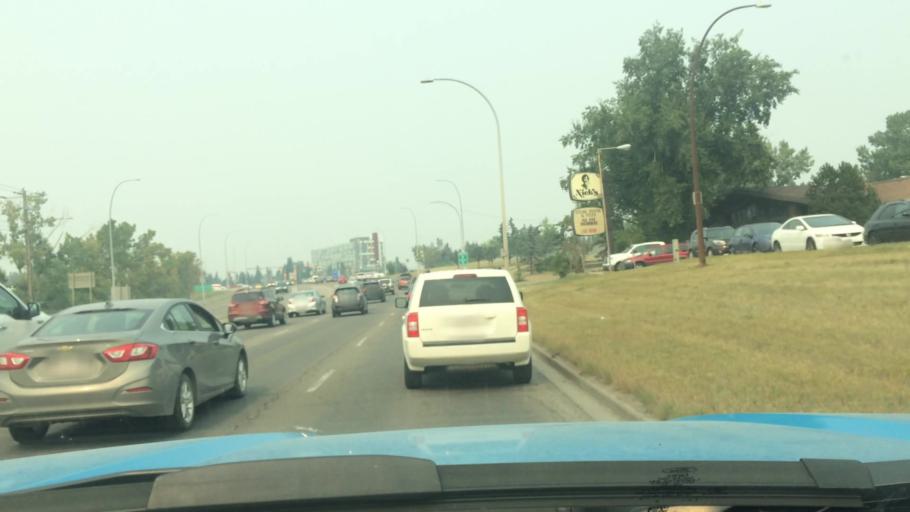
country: CA
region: Alberta
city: Calgary
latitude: 51.0716
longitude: -114.1180
